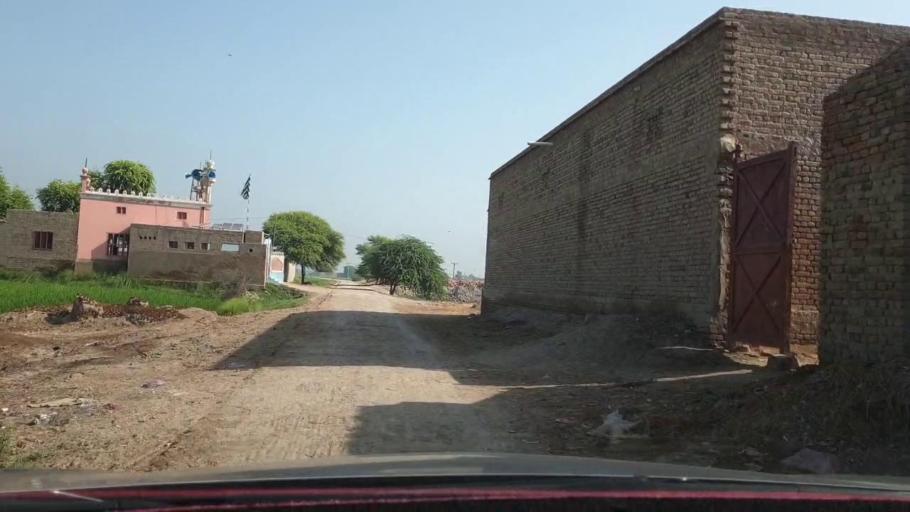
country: PK
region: Sindh
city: Nasirabad
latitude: 27.4781
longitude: 67.9252
